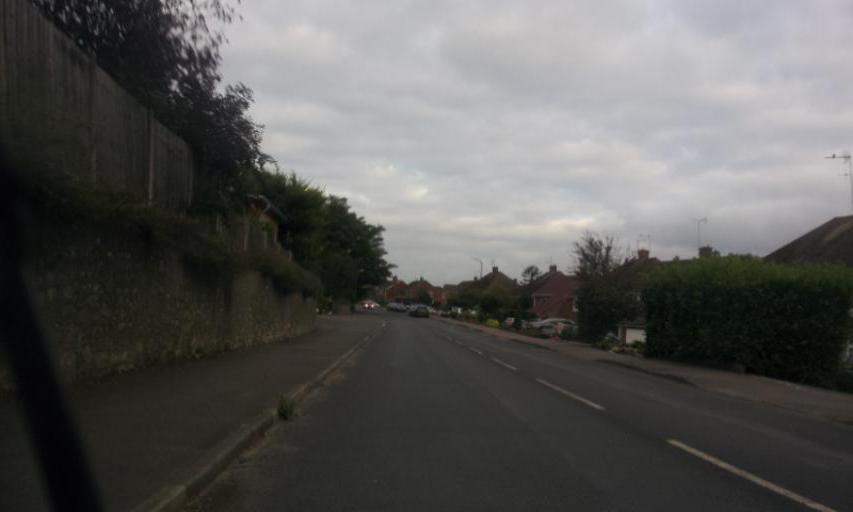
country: GB
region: England
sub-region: Kent
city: Aylesford
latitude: 51.2684
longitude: 0.4721
